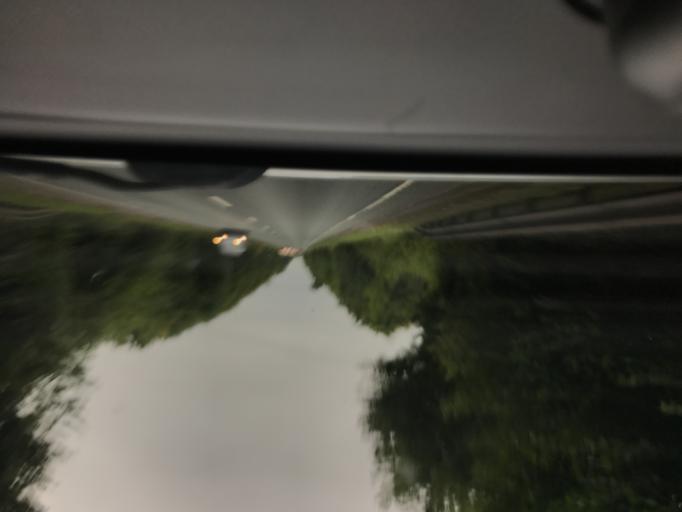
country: GB
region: England
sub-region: Cheshire West and Chester
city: Northwich
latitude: 53.2370
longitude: -2.5027
